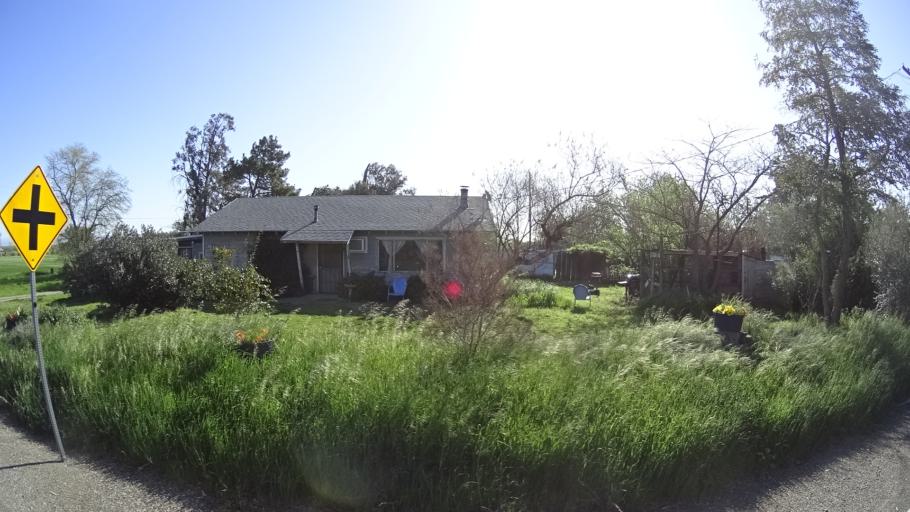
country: US
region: California
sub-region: Glenn County
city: Orland
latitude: 39.7952
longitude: -122.1041
